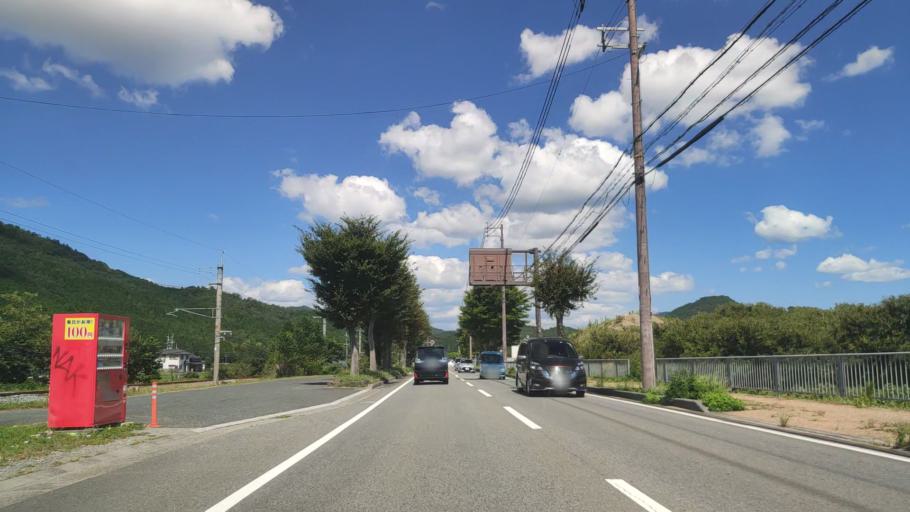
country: JP
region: Kyoto
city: Fukuchiyama
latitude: 35.1761
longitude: 135.1186
